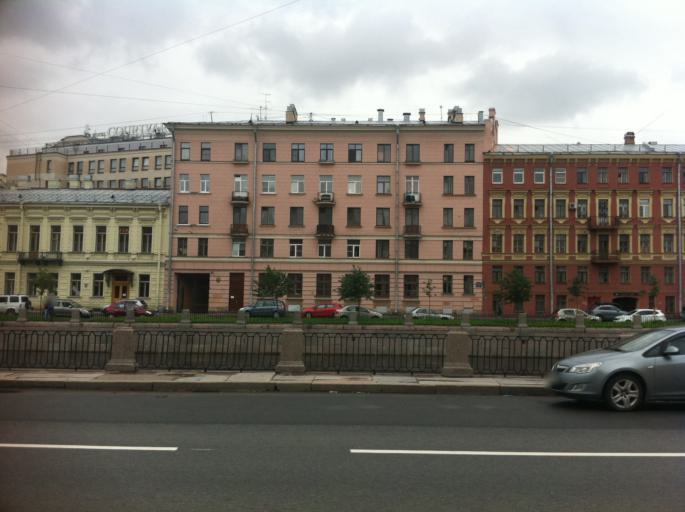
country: RU
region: St.-Petersburg
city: Admiralteisky
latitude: 59.9192
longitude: 30.2831
